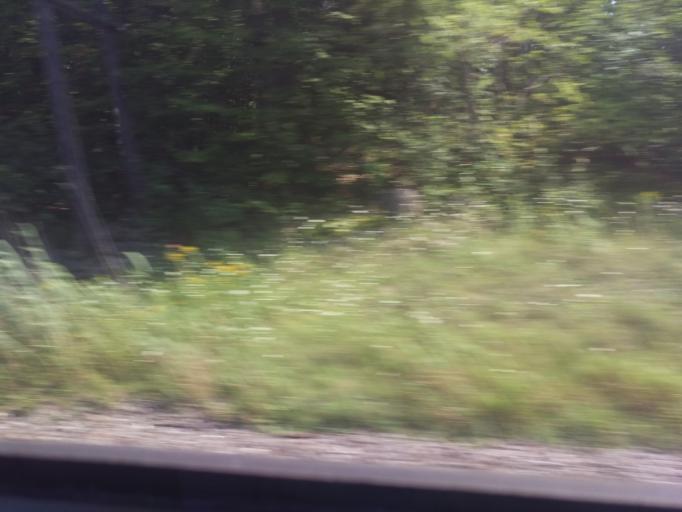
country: US
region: New York
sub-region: Jefferson County
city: Alexandria Bay
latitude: 44.4496
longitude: -75.9378
